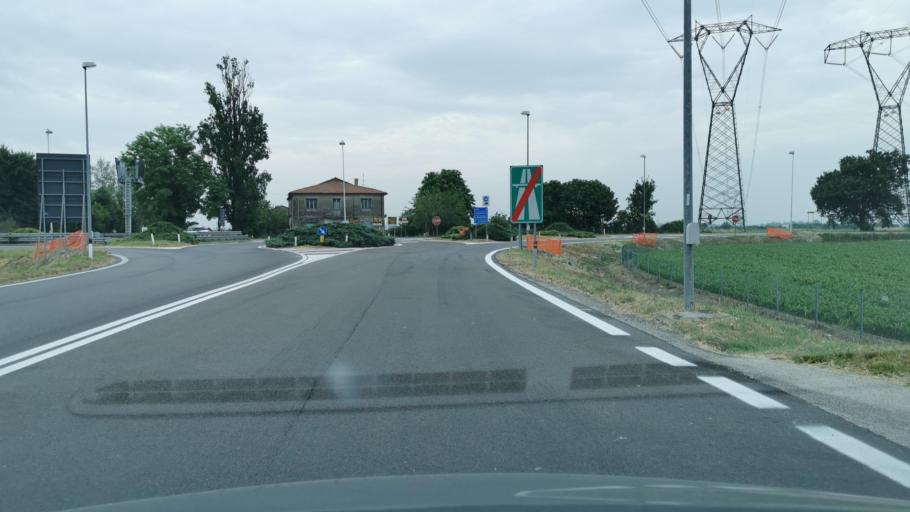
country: IT
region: Emilia-Romagna
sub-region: Provincia di Ravenna
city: Fornace Zarattini
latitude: 44.4138
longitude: 12.1267
